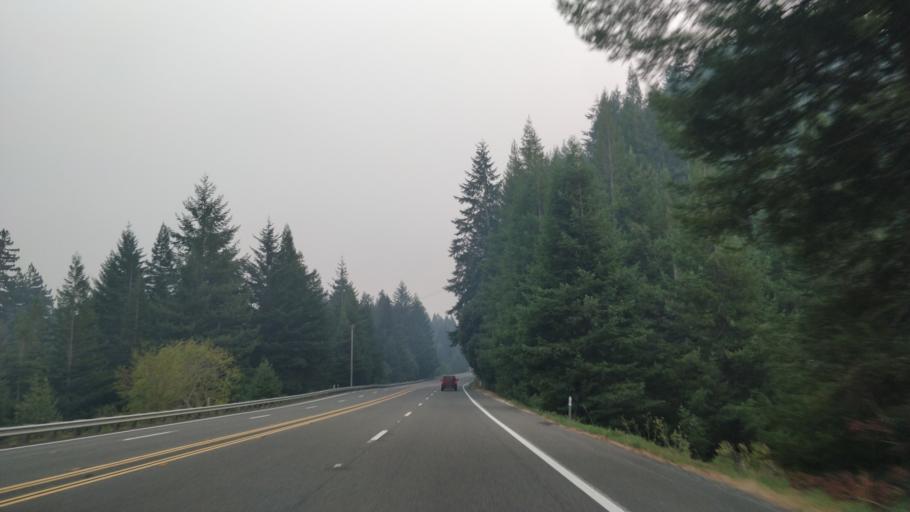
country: US
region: California
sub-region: Humboldt County
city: Rio Dell
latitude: 40.3834
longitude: -123.9290
